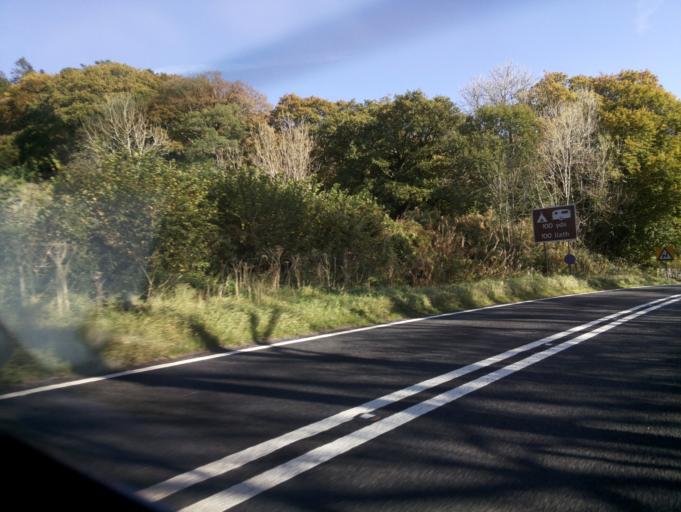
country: GB
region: Wales
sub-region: Merthyr Tydfil County Borough
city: Merthyr Tydfil
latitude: 51.7912
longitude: -3.4294
